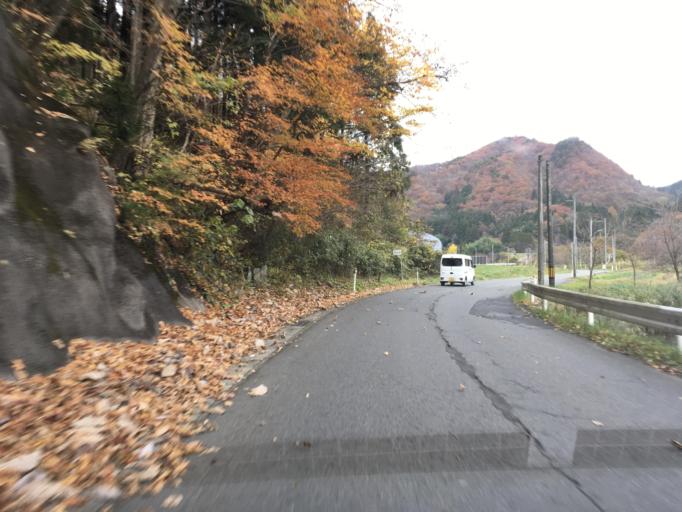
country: JP
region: Iwate
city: Mizusawa
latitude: 39.0921
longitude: 141.3468
